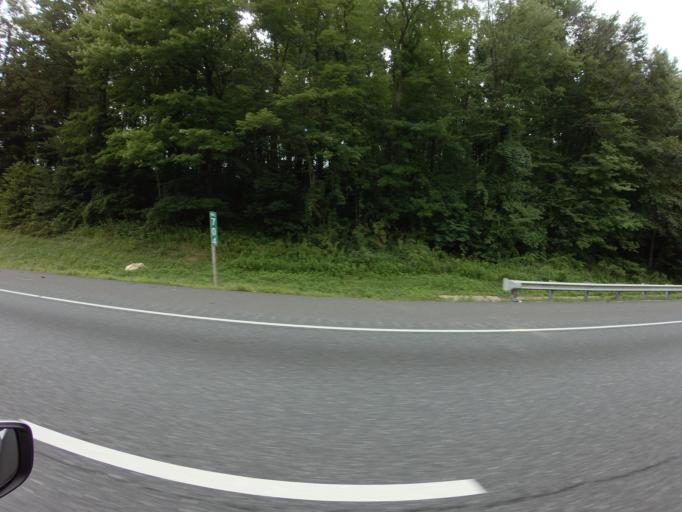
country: US
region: Maryland
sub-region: Baltimore County
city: Kingsville
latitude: 39.4174
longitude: -76.4081
